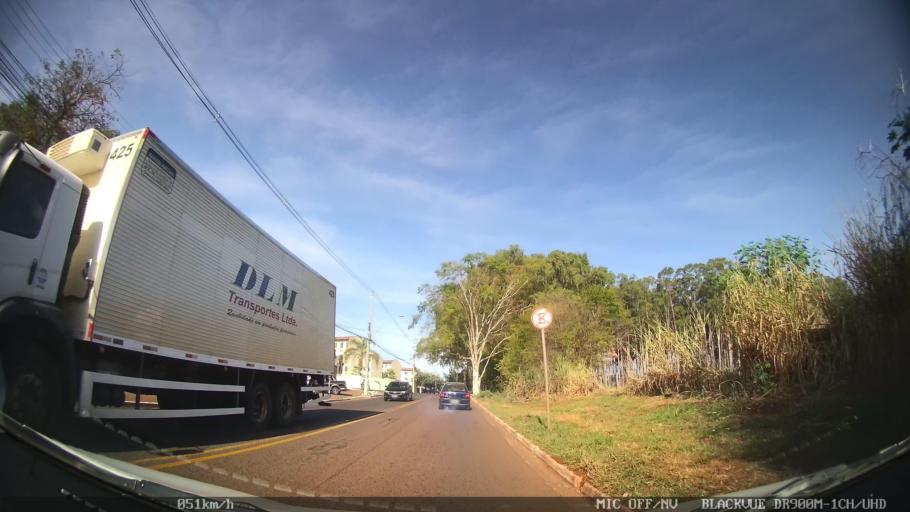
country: BR
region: Sao Paulo
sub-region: Ribeirao Preto
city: Ribeirao Preto
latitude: -21.2098
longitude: -47.8250
